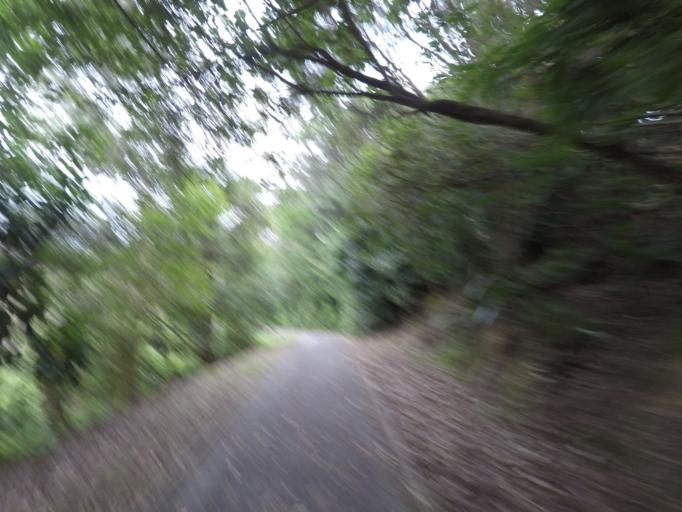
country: NZ
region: Auckland
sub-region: Auckland
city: Rosebank
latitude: -36.8736
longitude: 174.6961
